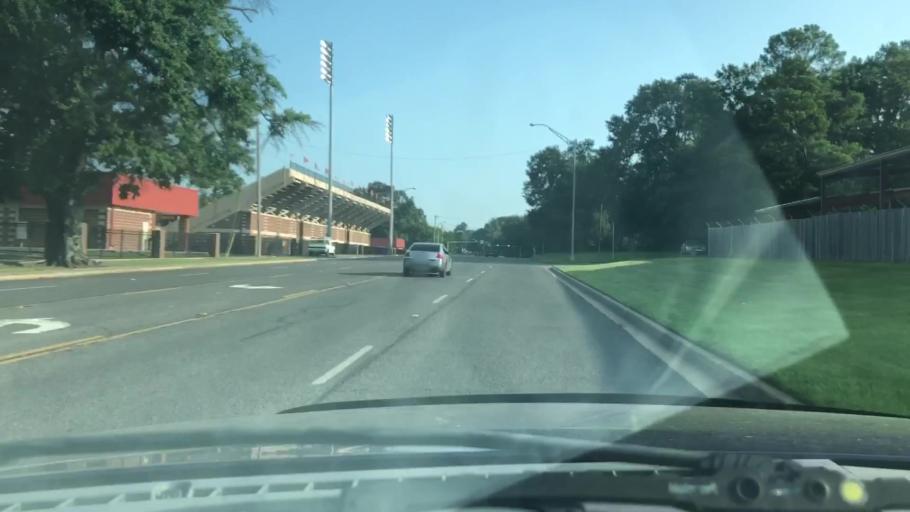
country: US
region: Texas
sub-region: Bowie County
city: Texarkana
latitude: 33.4267
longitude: -94.0614
